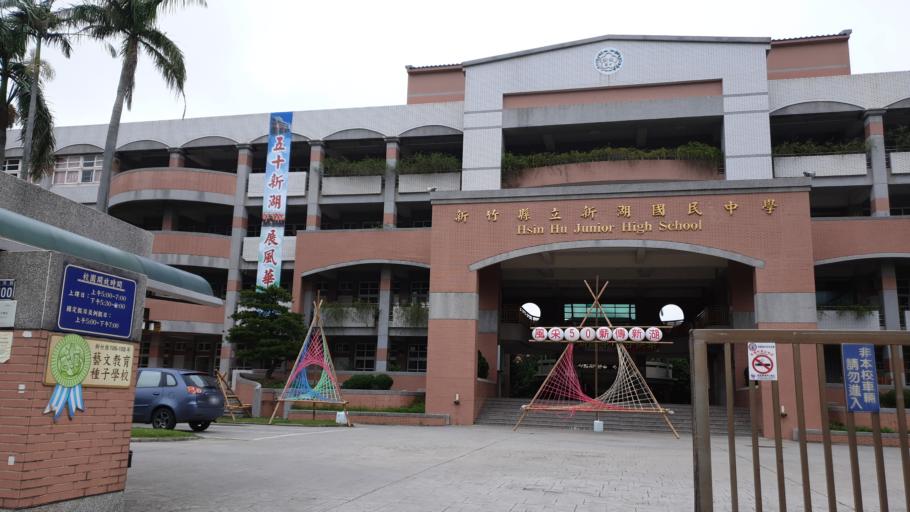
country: TW
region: Taiwan
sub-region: Hsinchu
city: Zhubei
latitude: 24.9027
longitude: 121.0359
